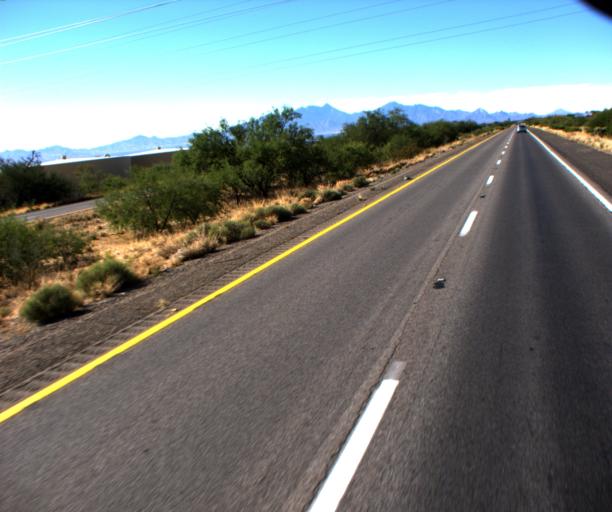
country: US
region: Arizona
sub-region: Pima County
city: Sahuarita
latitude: 31.9728
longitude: -110.9899
